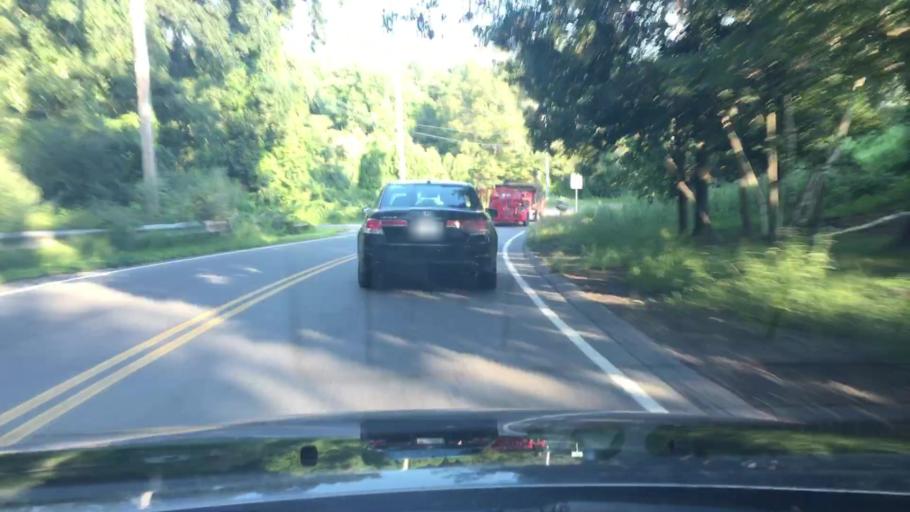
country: US
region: Massachusetts
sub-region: Worcester County
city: Westborough
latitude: 42.2514
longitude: -71.5902
